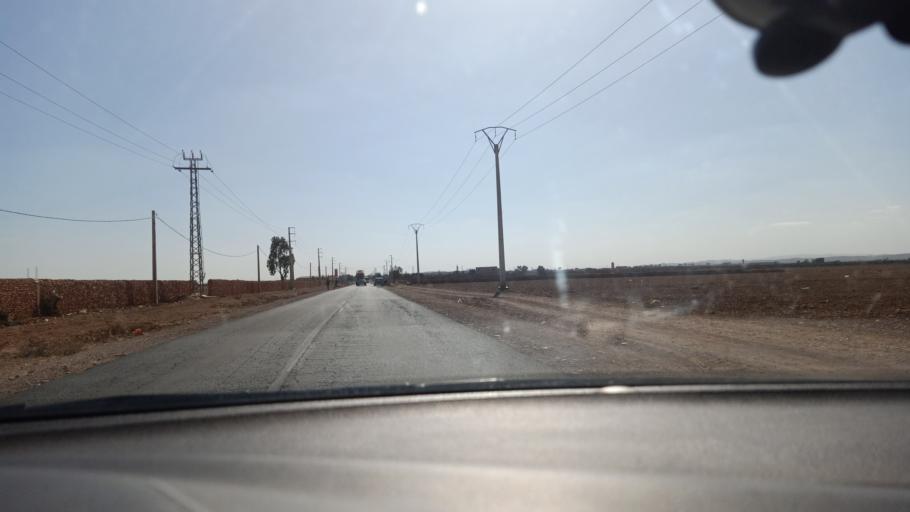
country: MA
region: Doukkala-Abda
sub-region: Safi
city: Youssoufia
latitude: 32.1099
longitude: -8.6087
